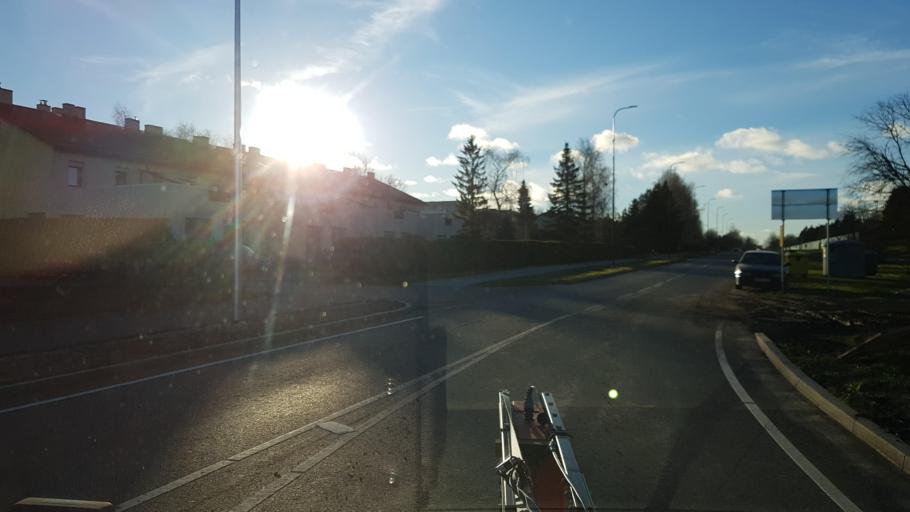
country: EE
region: Harju
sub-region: Saue linn
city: Saue
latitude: 59.3286
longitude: 24.5629
